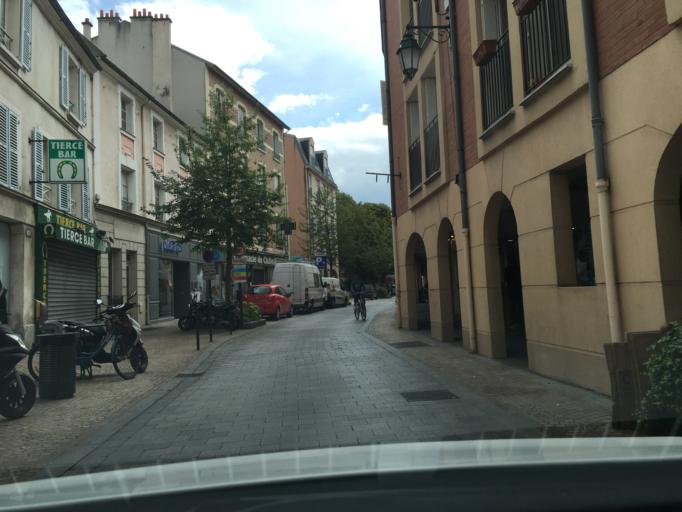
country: FR
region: Ile-de-France
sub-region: Departement des Hauts-de-Seine
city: Rueil-Malmaison
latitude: 48.8755
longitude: 2.1810
